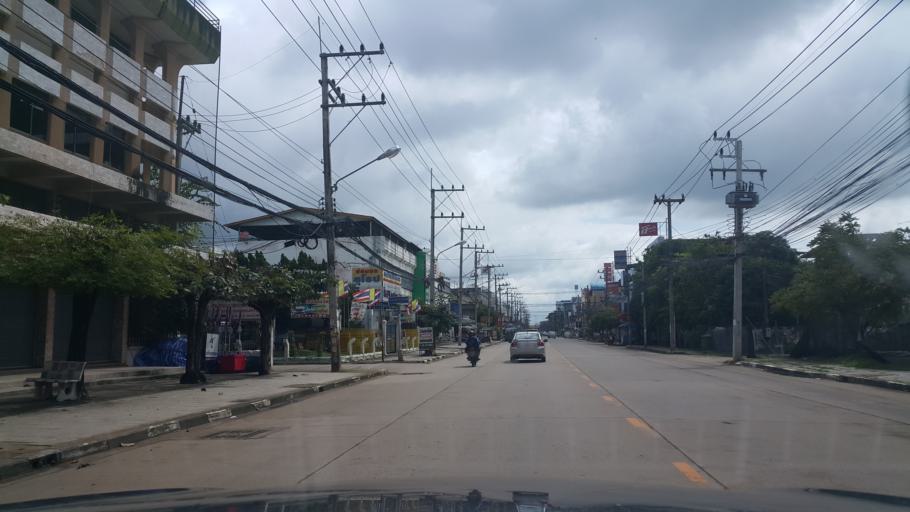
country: TH
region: Uttaradit
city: Uttaradit
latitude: 17.6110
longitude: 100.0854
